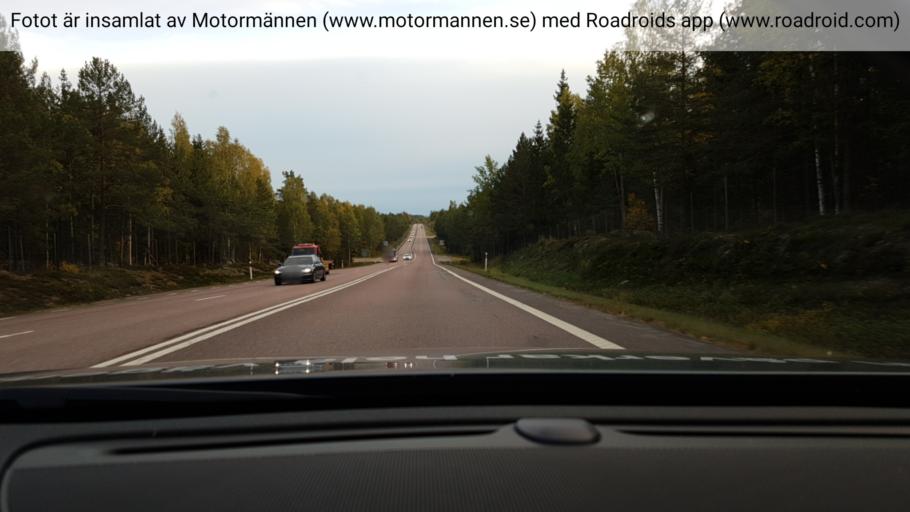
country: SE
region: Gaevleborg
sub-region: Nordanstigs Kommun
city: Bergsjoe
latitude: 61.8930
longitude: 17.1881
